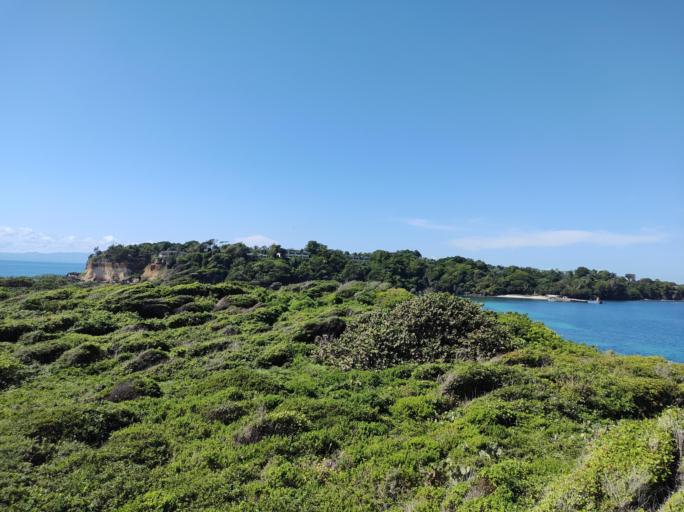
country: DO
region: Samana
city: Samana
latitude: 19.1695
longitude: -69.2703
